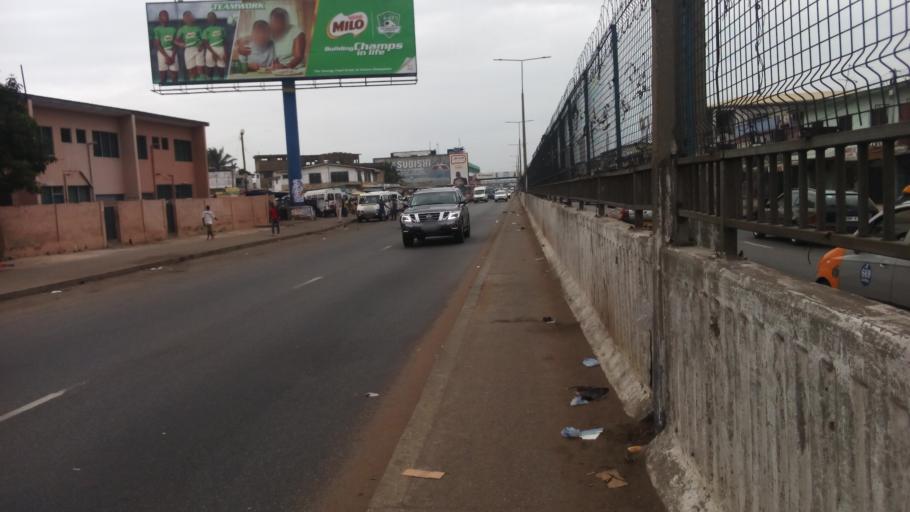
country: GH
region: Greater Accra
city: Accra
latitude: 5.5674
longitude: -0.2394
